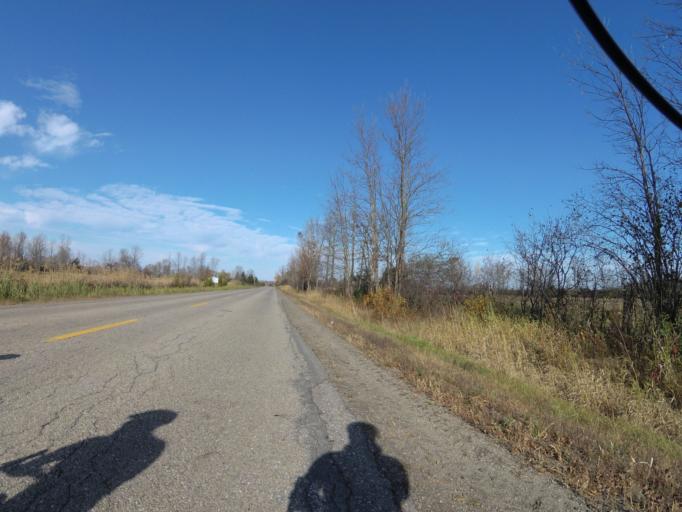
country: CA
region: Ontario
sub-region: Lanark County
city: Smiths Falls
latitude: 44.8229
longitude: -75.9456
